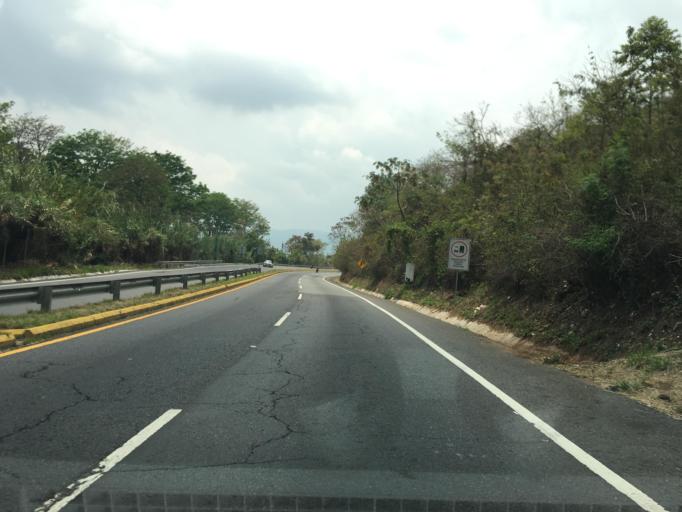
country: GT
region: Guatemala
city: Fraijanes
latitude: 14.4009
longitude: -90.4708
